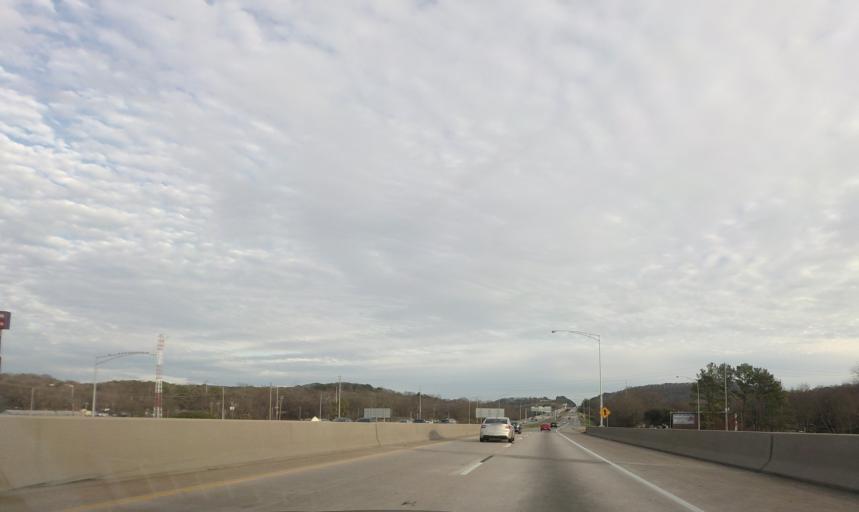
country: US
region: Alabama
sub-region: Jefferson County
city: Irondale
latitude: 33.5457
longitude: -86.7428
